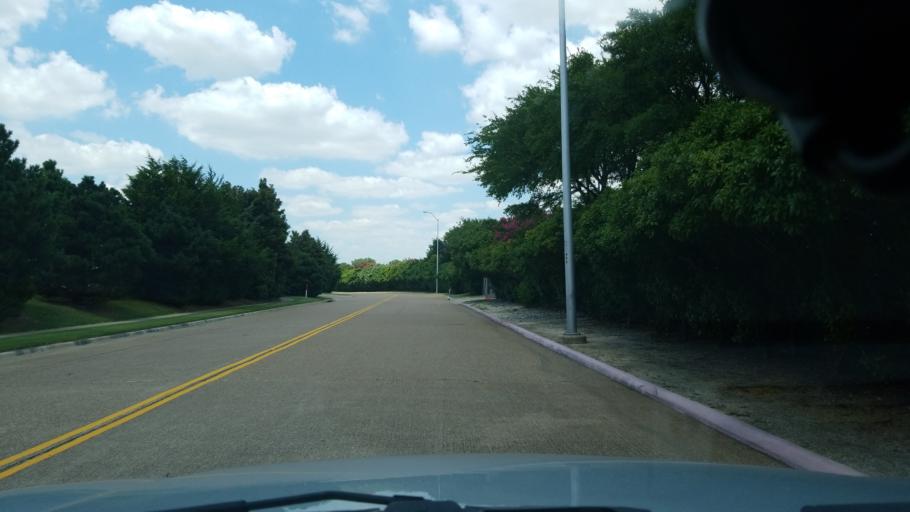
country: US
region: Texas
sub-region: Dallas County
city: Duncanville
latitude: 32.6812
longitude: -96.8802
